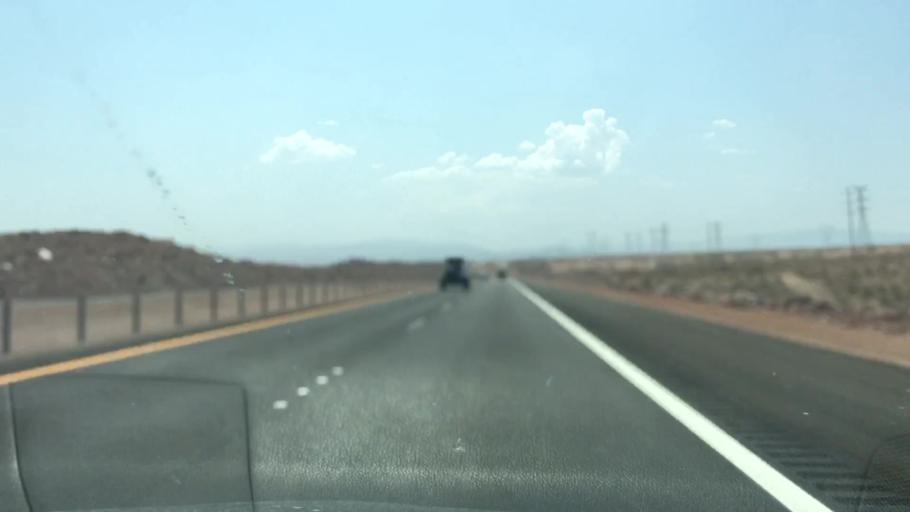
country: US
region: Nevada
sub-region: Clark County
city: Boulder City
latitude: 35.9622
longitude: -114.7994
